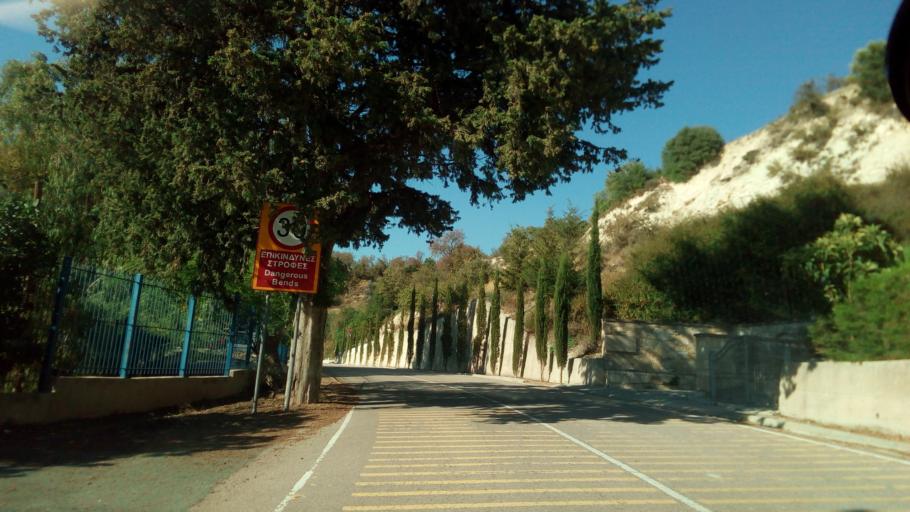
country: CY
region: Limassol
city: Pissouri
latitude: 34.8042
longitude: 32.6498
